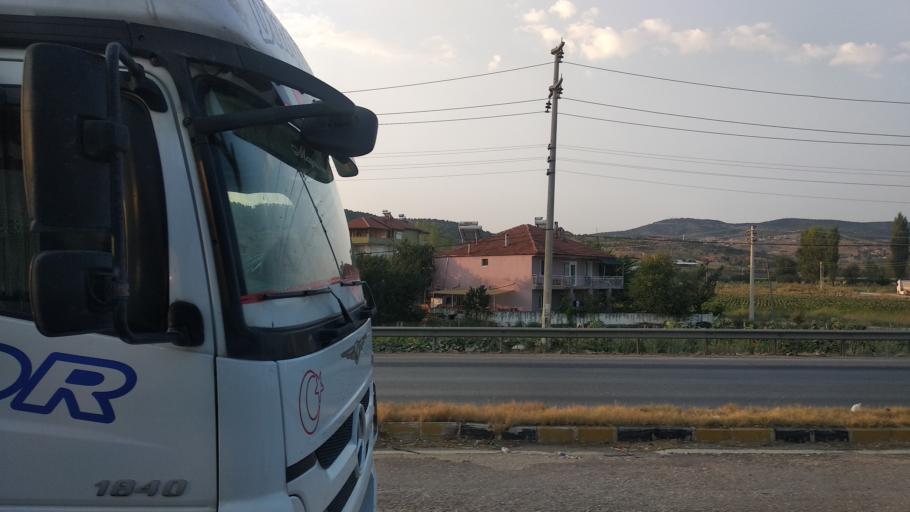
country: TR
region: Manisa
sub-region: Kula
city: Kula
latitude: 38.5425
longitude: 28.6570
